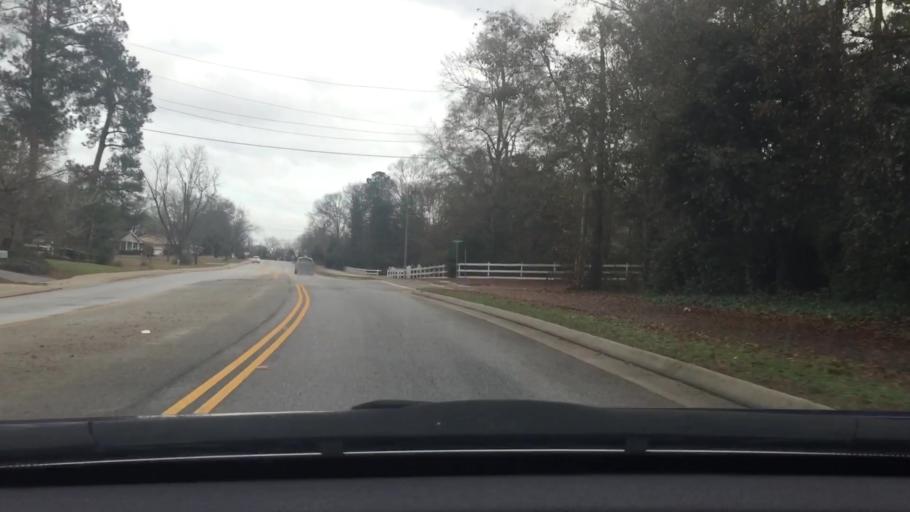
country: US
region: South Carolina
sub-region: Sumter County
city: South Sumter
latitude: 33.9173
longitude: -80.3915
